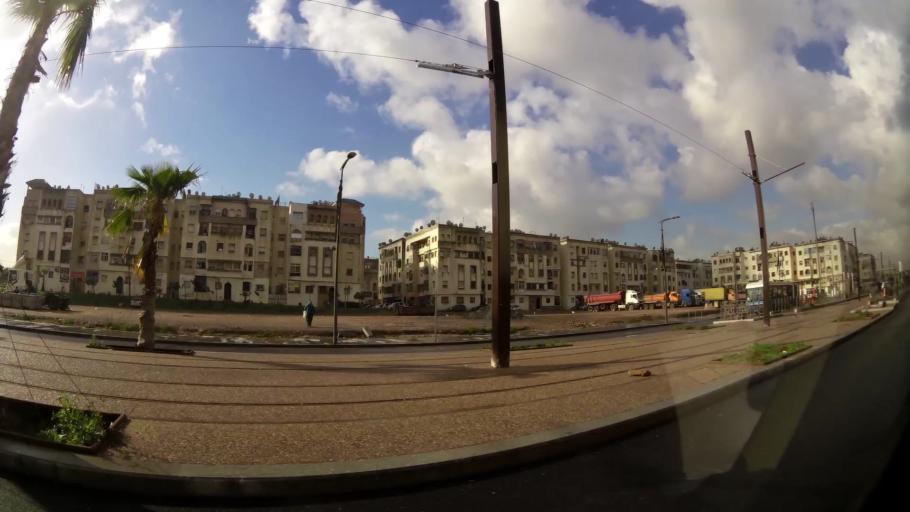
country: MA
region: Grand Casablanca
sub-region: Mediouna
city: Tit Mellil
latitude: 33.5996
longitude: -7.5322
